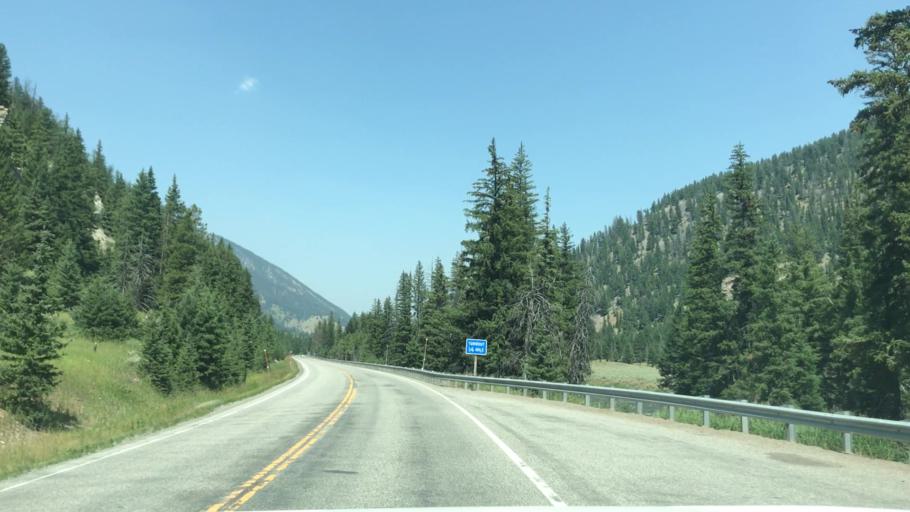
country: US
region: Montana
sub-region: Gallatin County
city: Big Sky
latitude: 45.0834
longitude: -111.2089
